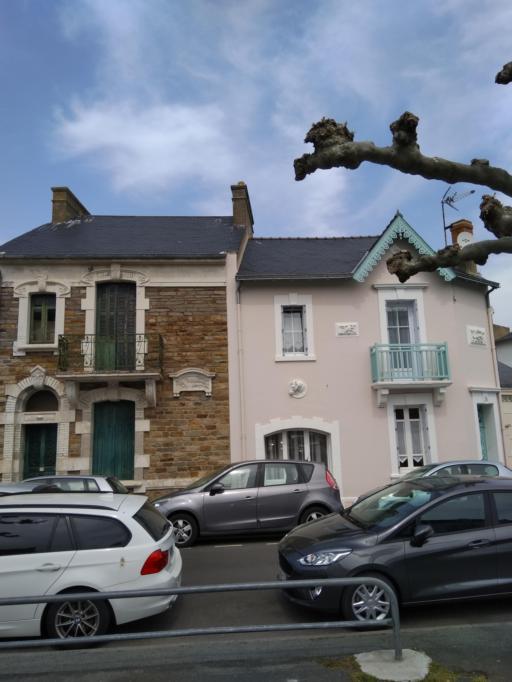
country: FR
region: Pays de la Loire
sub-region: Departement de la Vendee
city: Les Sables-d'Olonne
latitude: 46.4977
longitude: -1.7808
